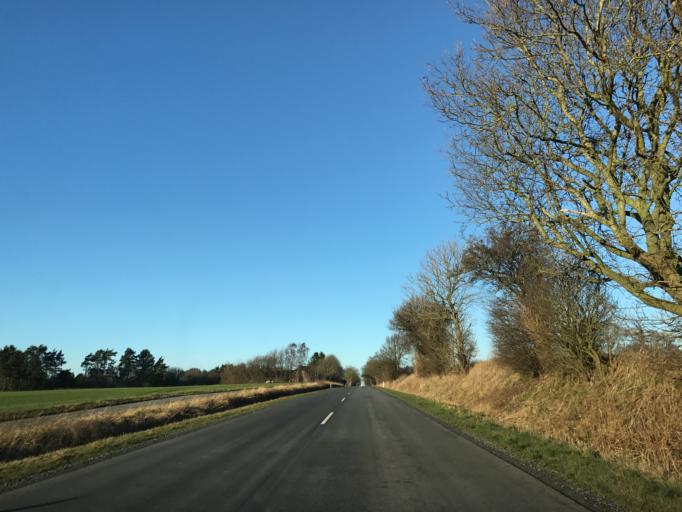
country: DK
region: South Denmark
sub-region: Haderslev Kommune
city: Haderslev
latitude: 55.2159
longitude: 9.5030
